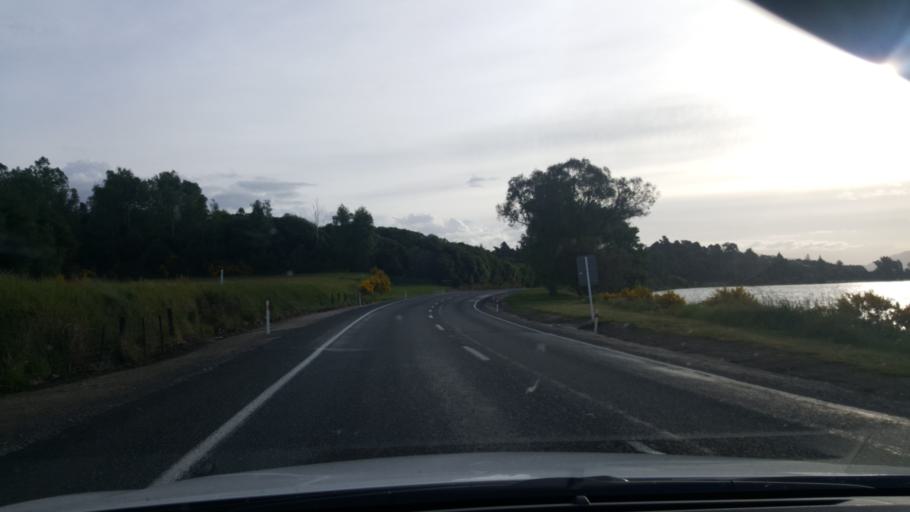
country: NZ
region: Waikato
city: Turangi
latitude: -38.9035
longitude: 175.9418
